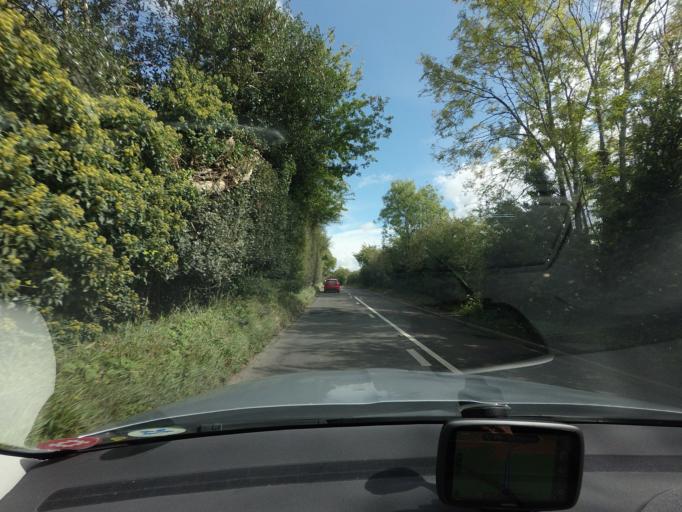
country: GB
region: England
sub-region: Kent
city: Borough Green
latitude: 51.2924
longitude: 0.2969
